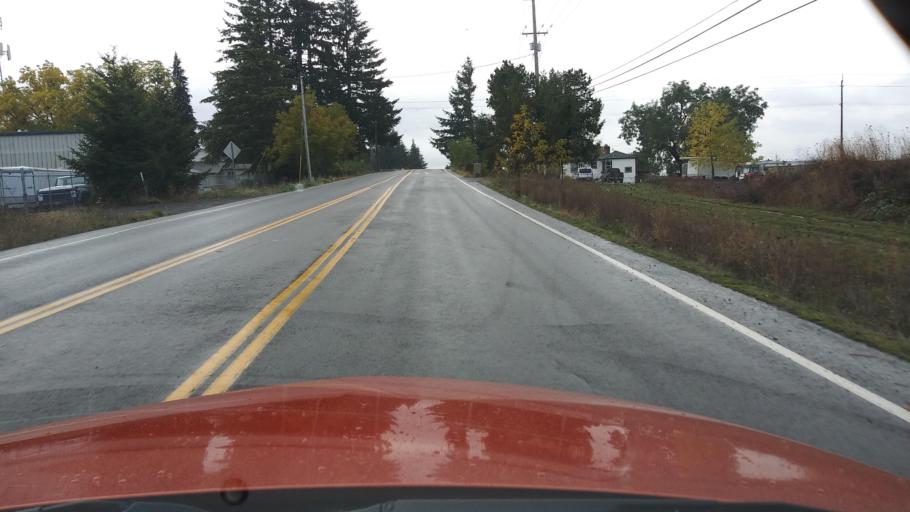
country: US
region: Oregon
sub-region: Washington County
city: North Plains
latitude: 45.5989
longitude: -123.0131
